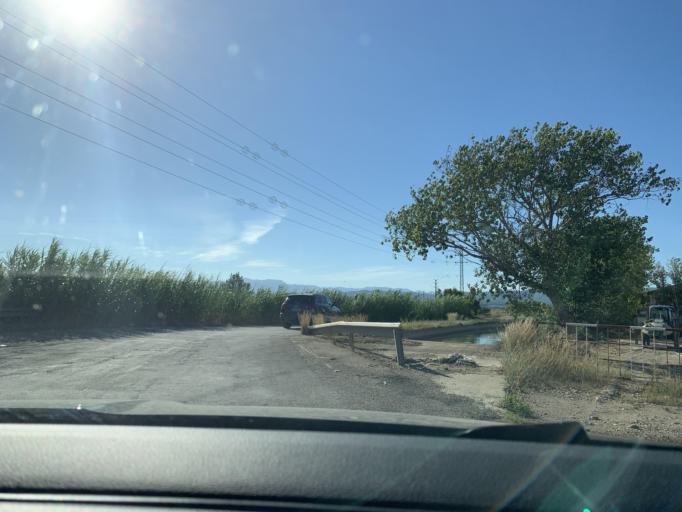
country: ES
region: Catalonia
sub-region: Provincia de Tarragona
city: Deltebre
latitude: 40.7574
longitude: 0.7123
